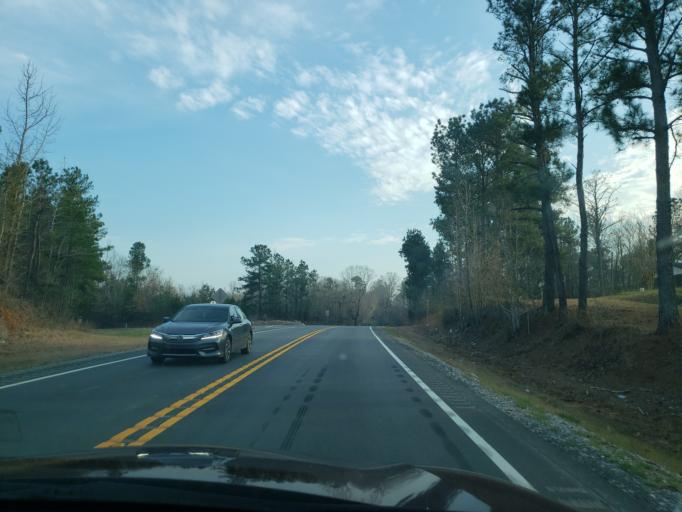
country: US
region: Alabama
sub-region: Hale County
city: Moundville
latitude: 32.8839
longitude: -87.6083
